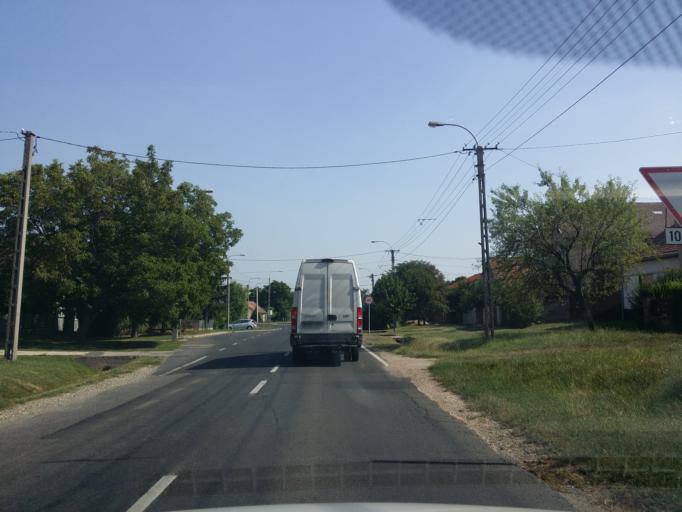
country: HU
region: Fejer
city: Mezofalva
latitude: 46.9305
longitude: 18.7895
